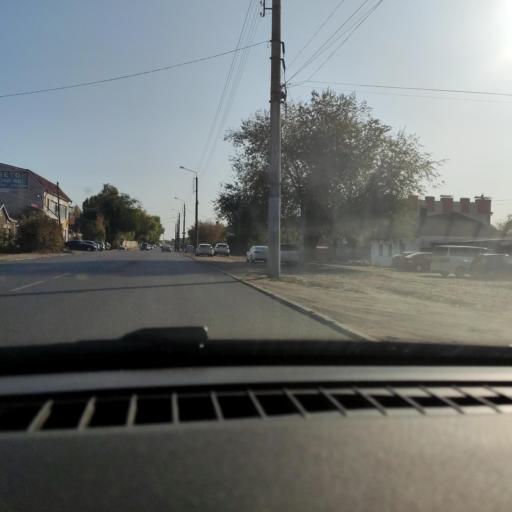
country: RU
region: Voronezj
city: Voronezh
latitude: 51.6315
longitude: 39.1747
